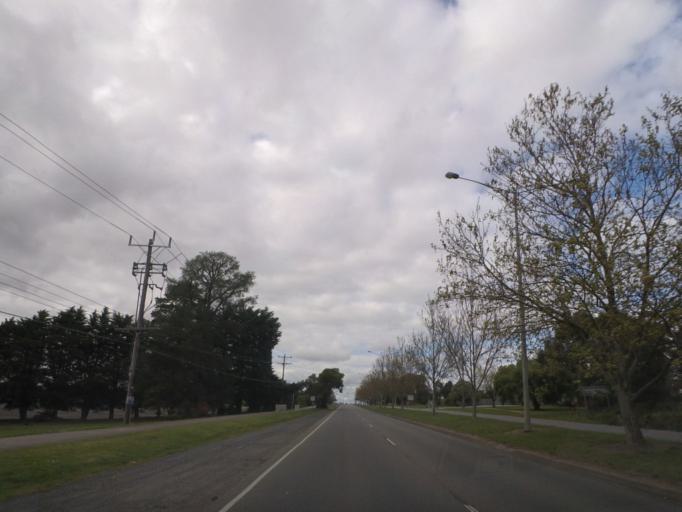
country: AU
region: Victoria
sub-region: Knox
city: Wantirna
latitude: -37.8513
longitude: 145.2234
